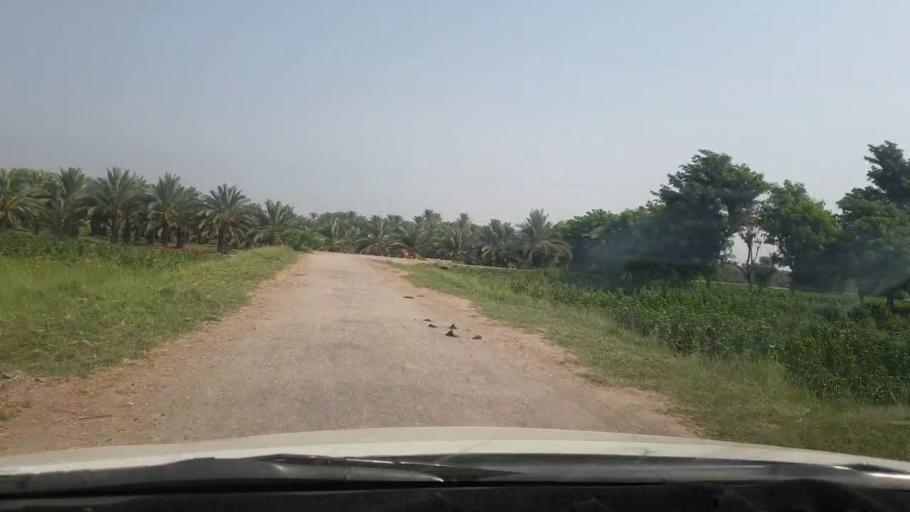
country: PK
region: Sindh
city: Rohri
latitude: 27.6144
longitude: 68.8976
